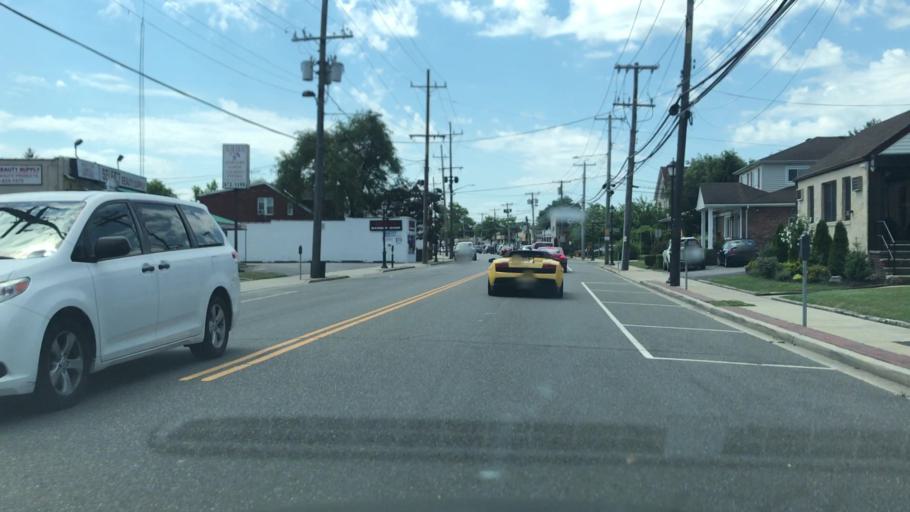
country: US
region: New York
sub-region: Nassau County
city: North Valley Stream
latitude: 40.6763
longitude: -73.7094
